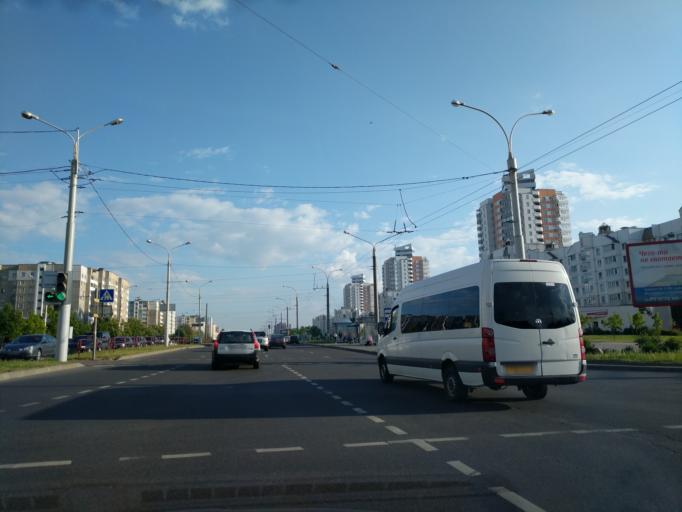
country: BY
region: Minsk
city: Zhdanovichy
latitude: 53.9161
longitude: 27.4368
